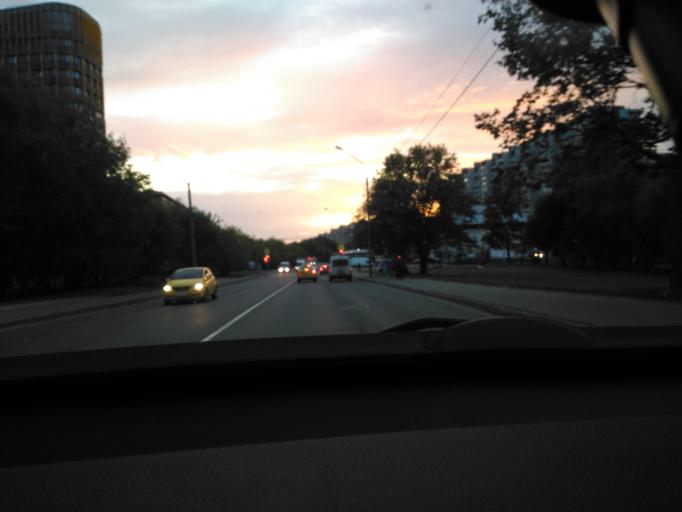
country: RU
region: Moscow
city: Vatutino
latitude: 55.8871
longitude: 37.6811
